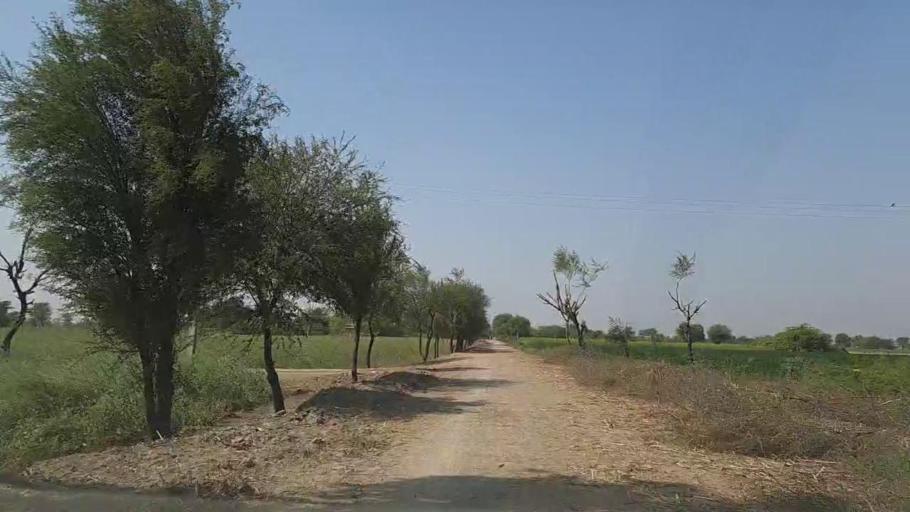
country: PK
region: Sindh
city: Samaro
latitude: 25.2269
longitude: 69.3939
